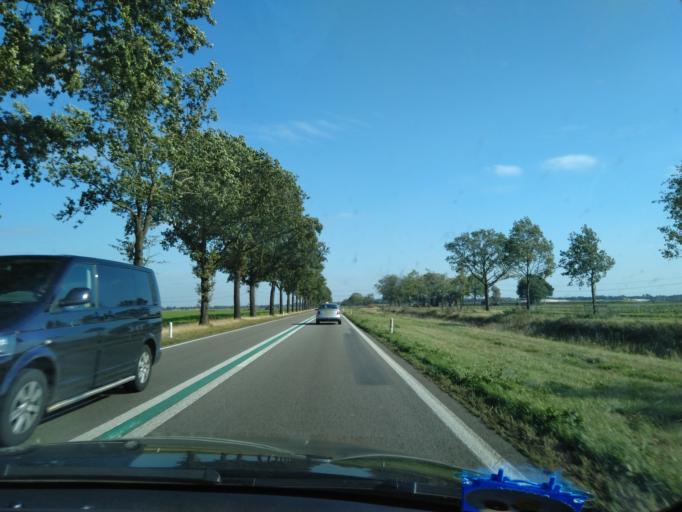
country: NL
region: Groningen
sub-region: Gemeente Veendam
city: Veendam
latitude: 53.0910
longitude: 6.9318
